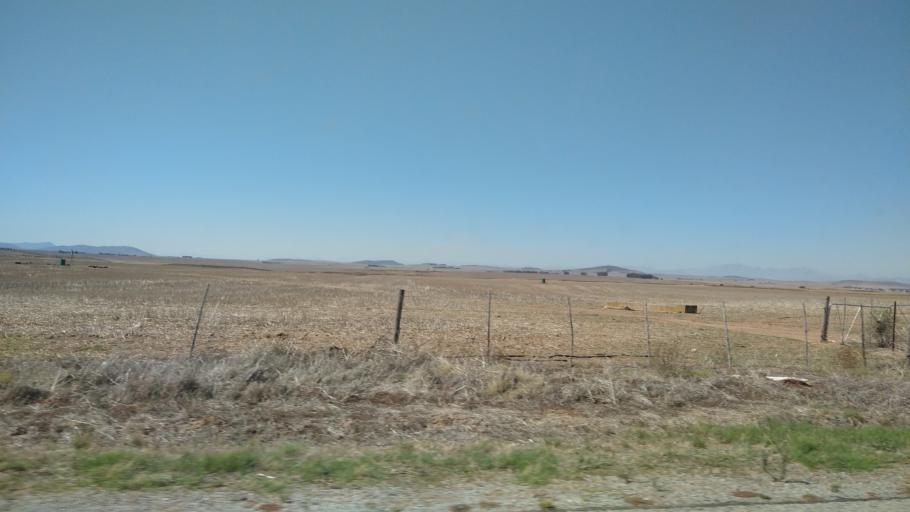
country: ZA
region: Western Cape
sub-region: West Coast District Municipality
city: Moorreesburg
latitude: -33.2276
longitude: 18.5537
